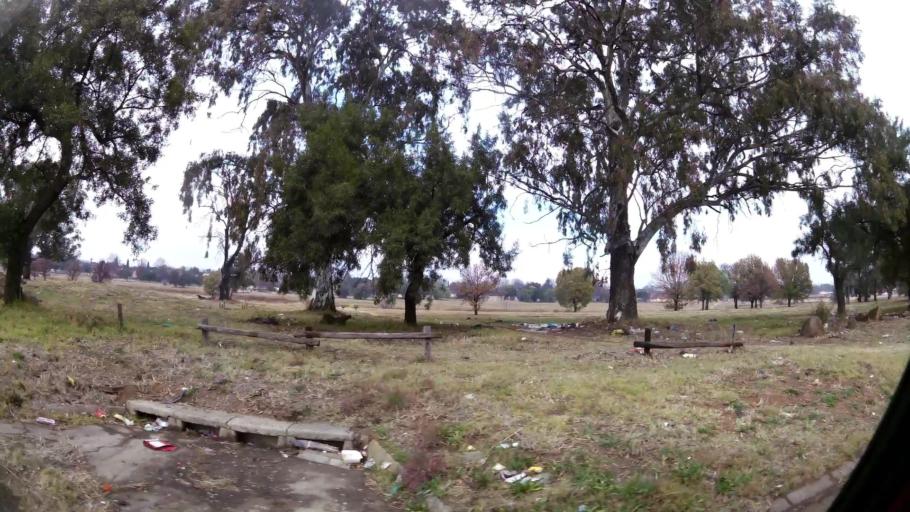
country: ZA
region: Gauteng
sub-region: Sedibeng District Municipality
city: Vanderbijlpark
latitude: -26.7124
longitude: 27.8565
